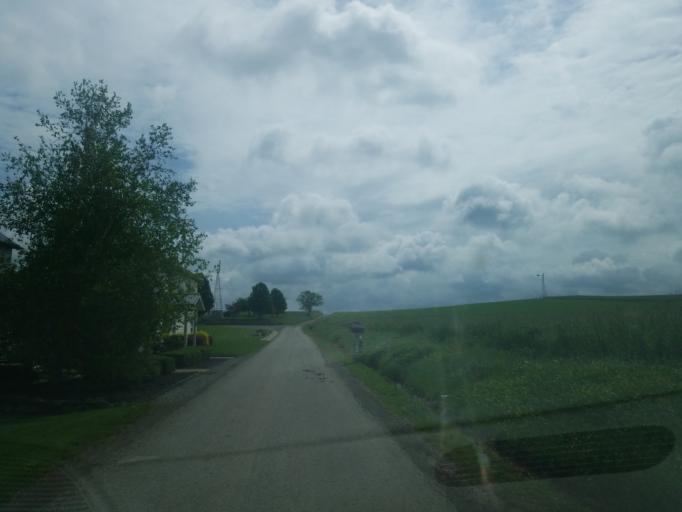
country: US
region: Ohio
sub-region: Tuscarawas County
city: Sugarcreek
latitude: 40.5156
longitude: -81.7674
